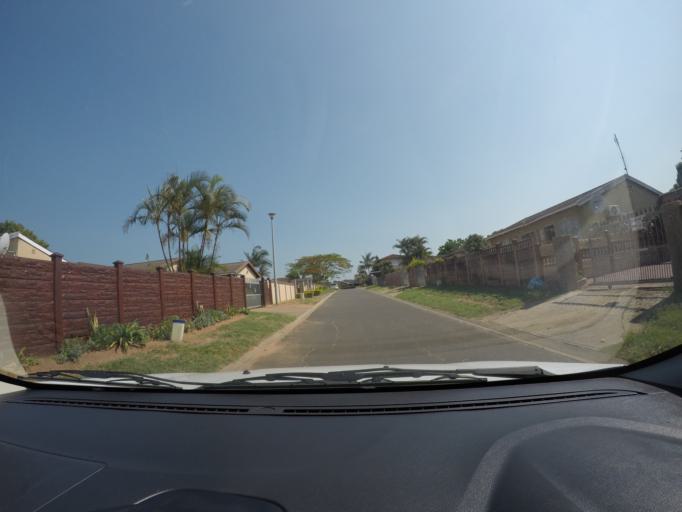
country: ZA
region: KwaZulu-Natal
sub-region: uThungulu District Municipality
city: Richards Bay
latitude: -28.7228
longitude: 32.0456
